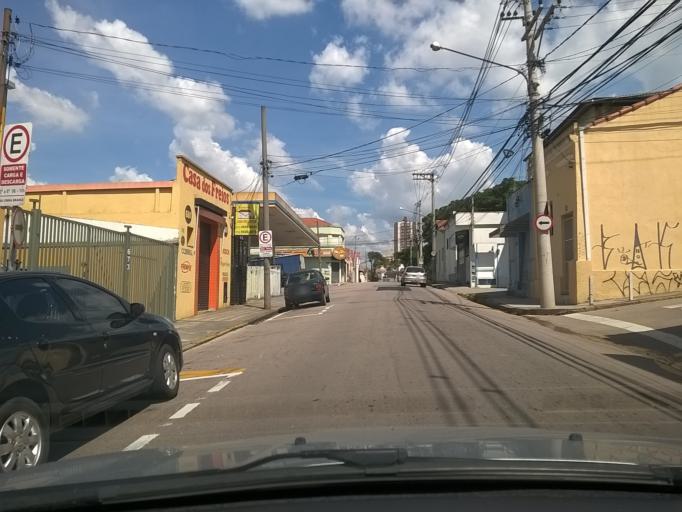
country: BR
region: Sao Paulo
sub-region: Jundiai
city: Jundiai
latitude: -23.1997
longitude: -46.8863
